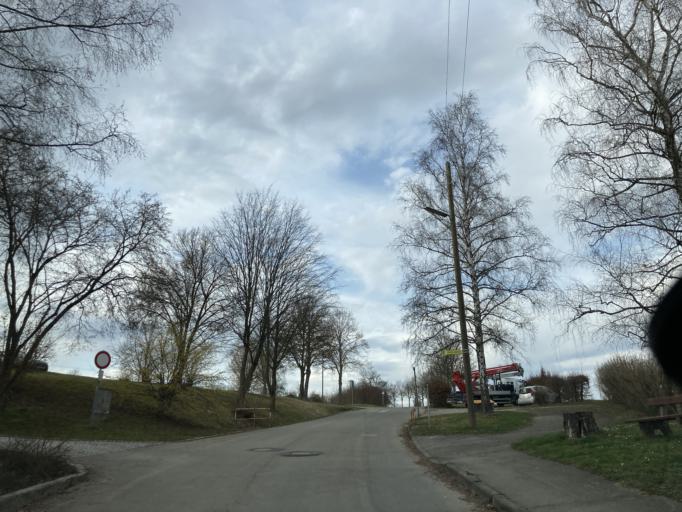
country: DE
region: Baden-Wuerttemberg
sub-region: Tuebingen Region
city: Dusslingen
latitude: 48.4541
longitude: 9.0517
